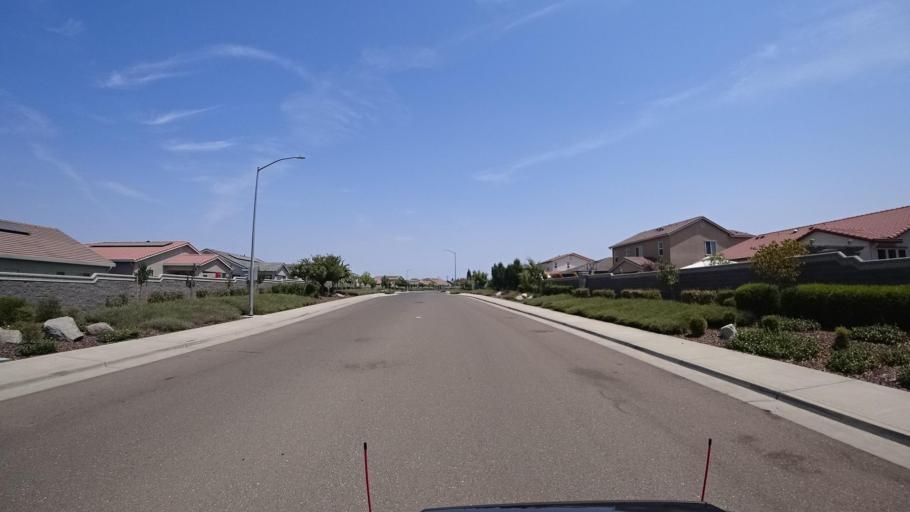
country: US
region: California
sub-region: Placer County
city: Rocklin
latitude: 38.8049
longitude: -121.2231
